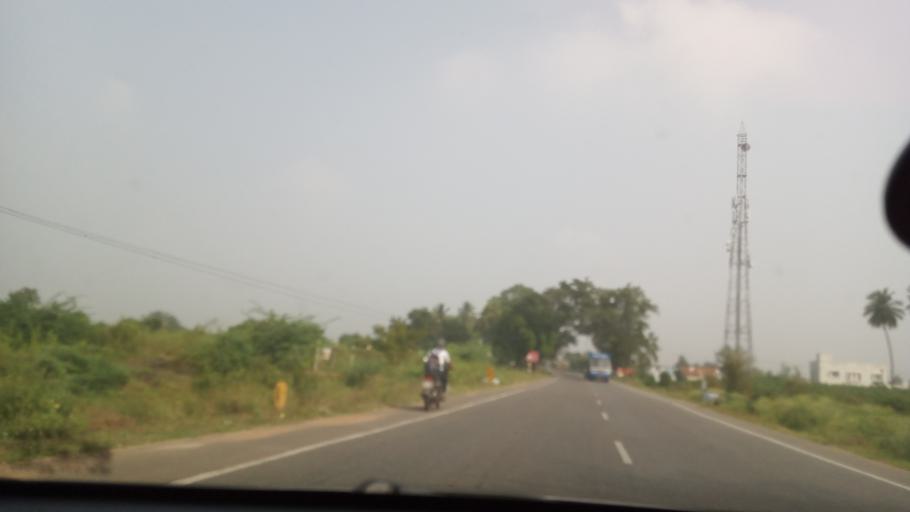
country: IN
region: Tamil Nadu
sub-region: Erode
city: Punjai Puliyampatti
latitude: 11.3800
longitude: 77.1725
